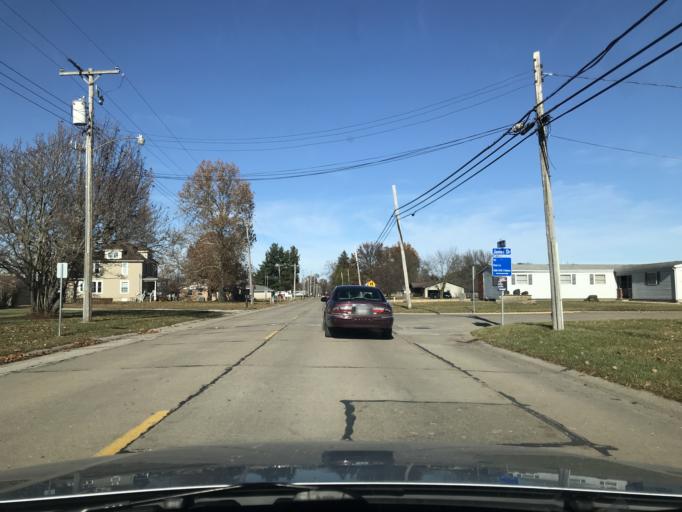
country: US
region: Illinois
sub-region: McDonough County
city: Macomb
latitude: 40.4411
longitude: -90.6709
